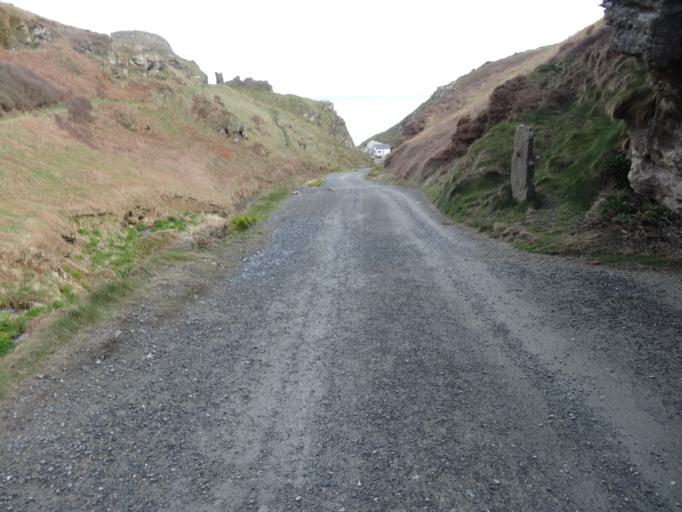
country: GB
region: England
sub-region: Cornwall
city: Tintagel
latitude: 50.6656
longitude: -4.7568
